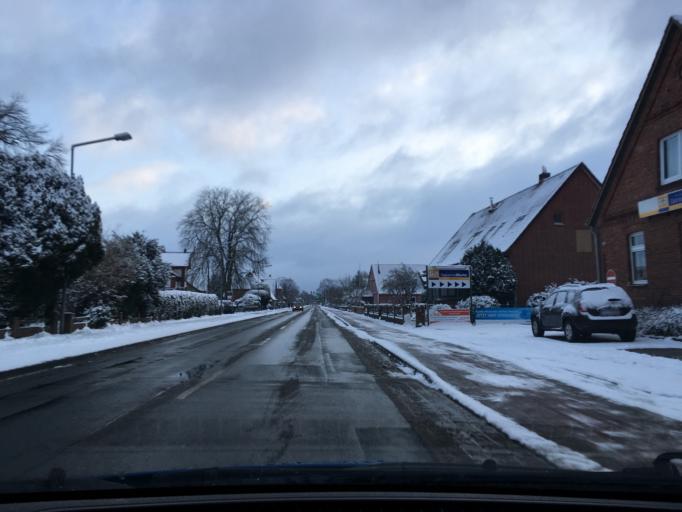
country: DE
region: Lower Saxony
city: Winsen
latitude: 53.3447
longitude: 10.2052
